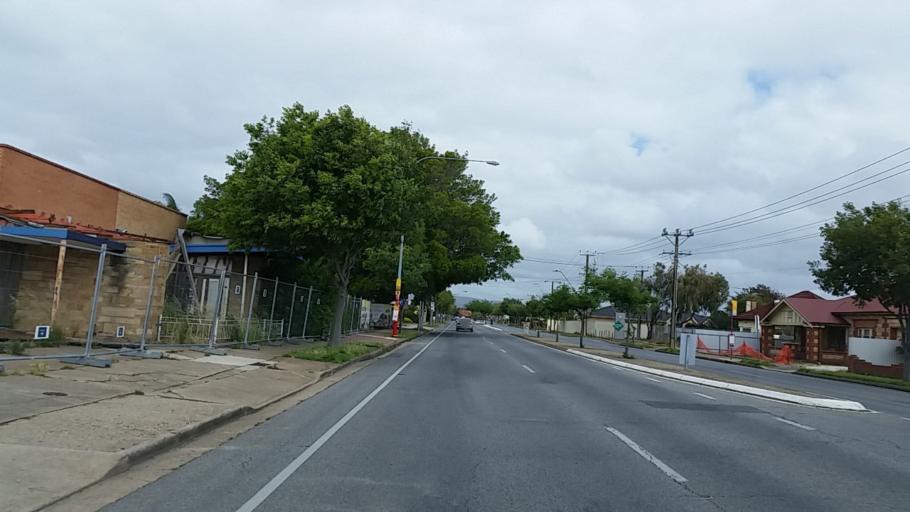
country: AU
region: South Australia
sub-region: Charles Sturt
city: Findon
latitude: -34.9021
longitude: 138.5424
